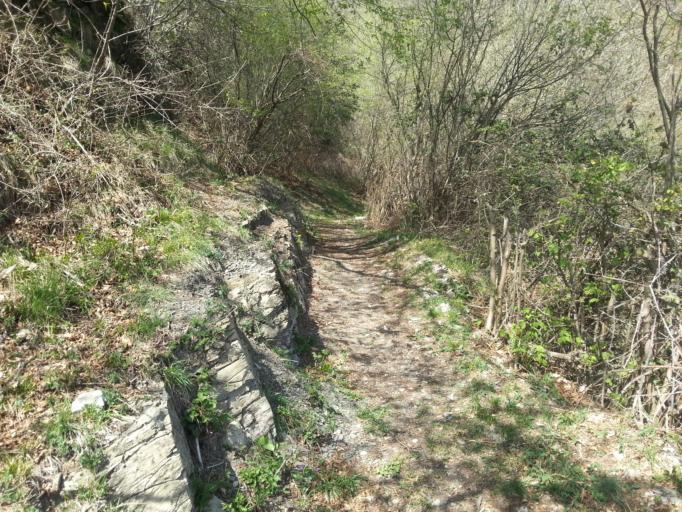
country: IT
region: Lombardy
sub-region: Provincia di Como
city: Mezzegra
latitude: 45.9966
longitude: 9.2067
